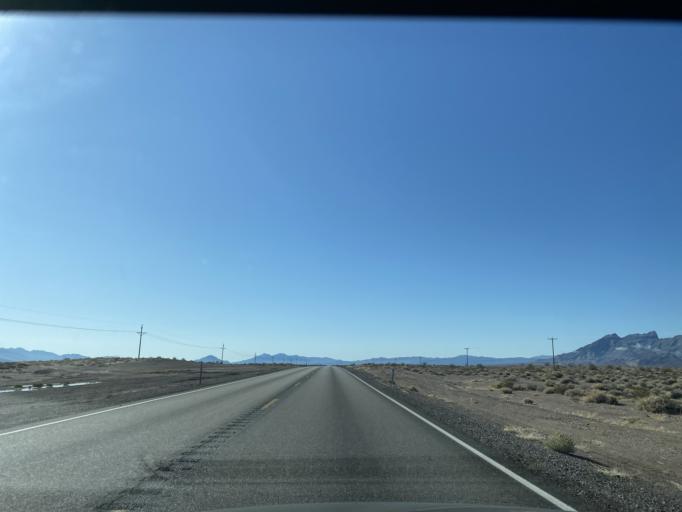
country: US
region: Nevada
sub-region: Nye County
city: Pahrump
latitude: 36.4573
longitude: -116.4218
